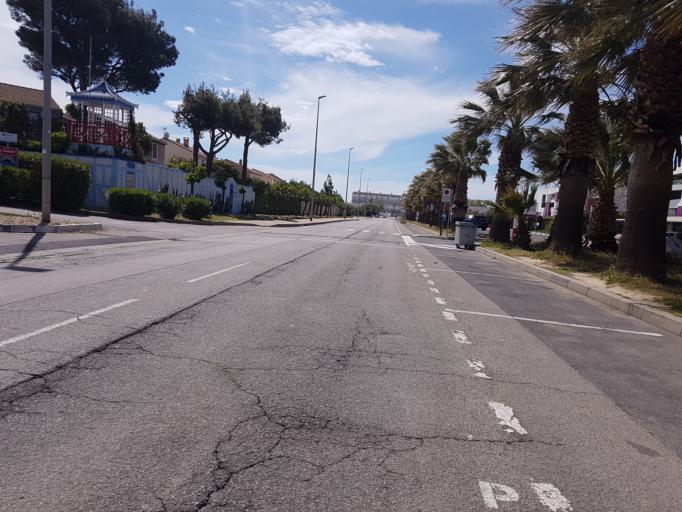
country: FR
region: Languedoc-Roussillon
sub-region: Departement de l'Herault
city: Palavas-les-Flots
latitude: 43.5337
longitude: 3.9386
